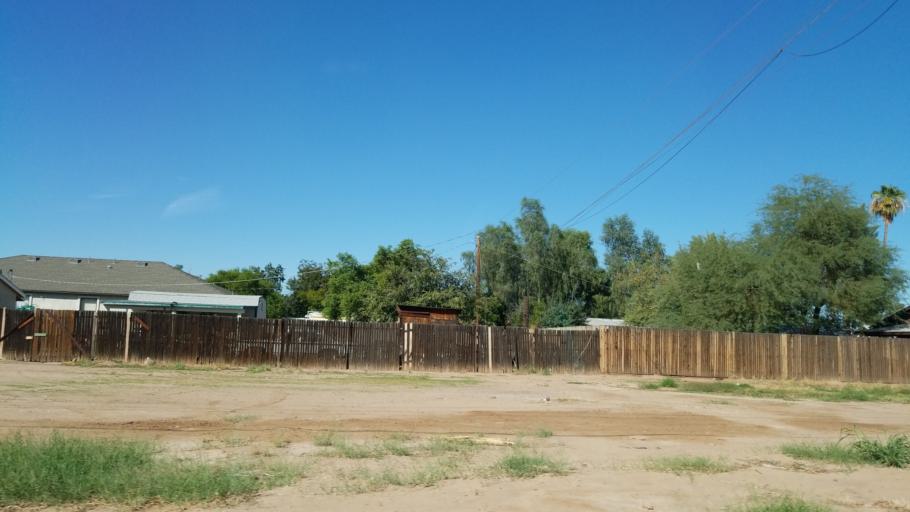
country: US
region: Arizona
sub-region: Maricopa County
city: Glendale
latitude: 33.5435
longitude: -112.1774
